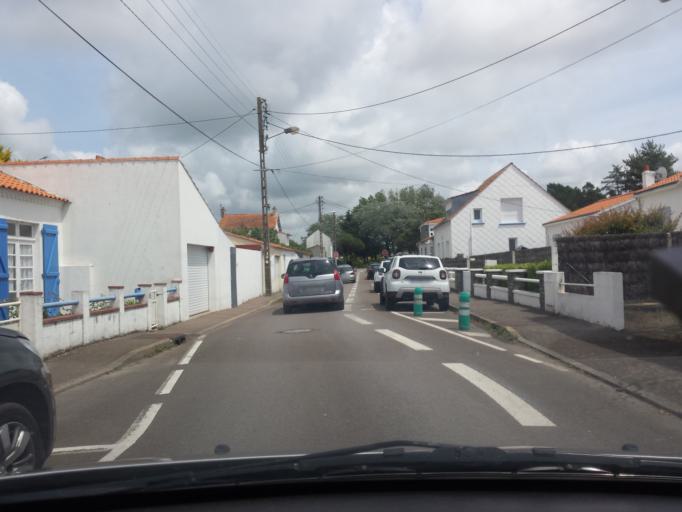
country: FR
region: Pays de la Loire
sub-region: Departement de la Vendee
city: Saint-Gilles-Croix-de-Vie
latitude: 46.6909
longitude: -1.9353
